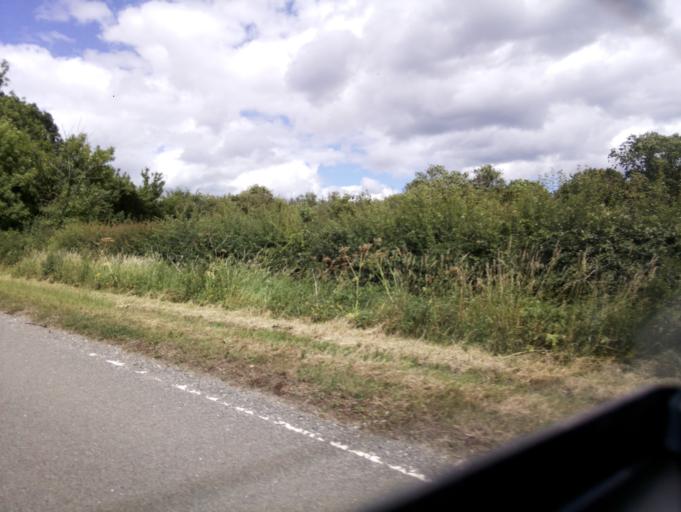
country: GB
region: England
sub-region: Nottinghamshire
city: East Leake
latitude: 52.8410
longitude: -1.1415
